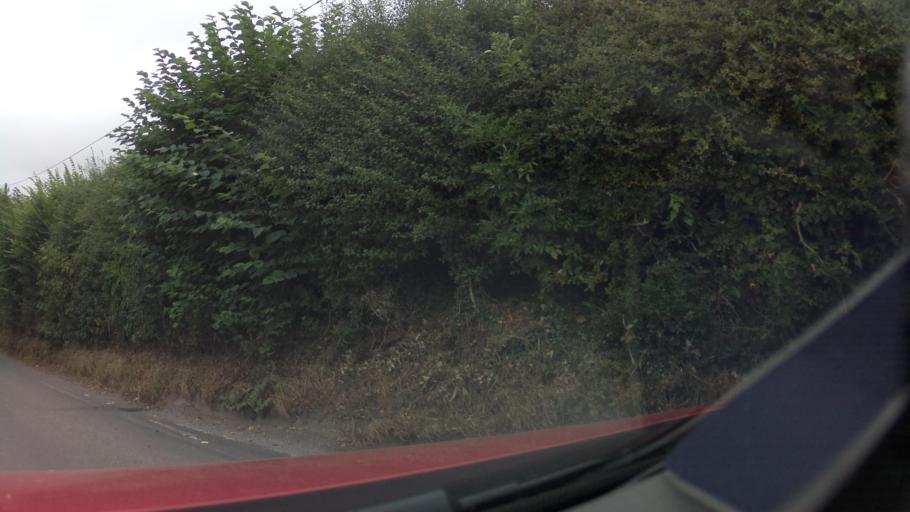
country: GB
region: England
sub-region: Derbyshire
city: Swadlincote
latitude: 52.7827
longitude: -1.5161
